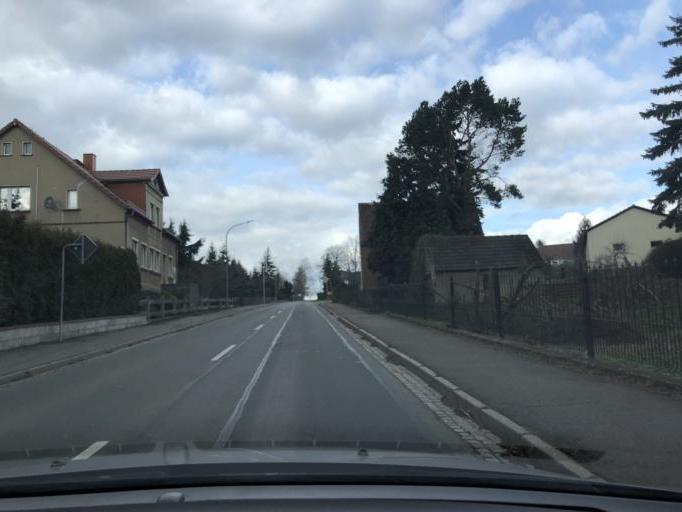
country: DE
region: Saxony
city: Dobeln
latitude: 51.1486
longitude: 13.0891
